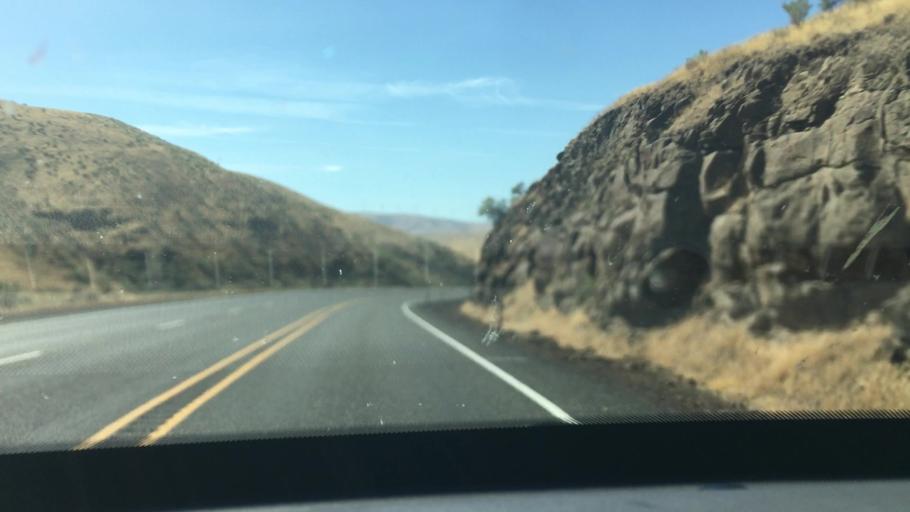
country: US
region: Oregon
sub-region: Sherman County
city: Moro
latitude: 45.6405
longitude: -120.7823
